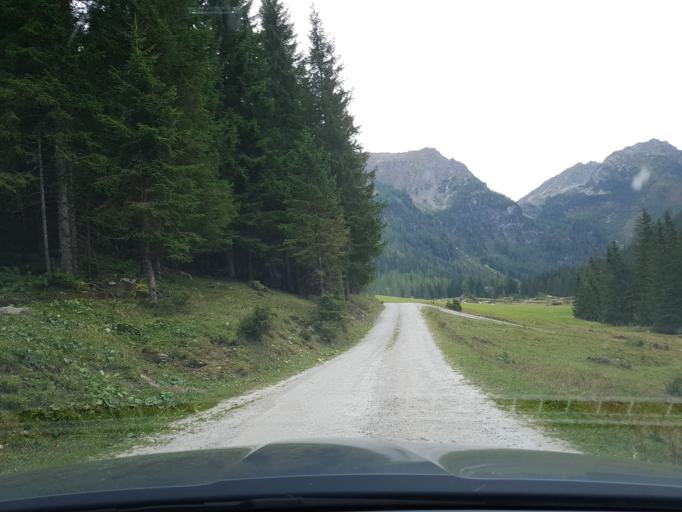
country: AT
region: Salzburg
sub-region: Politischer Bezirk Sankt Johann im Pongau
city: Untertauern
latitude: 47.2993
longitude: 13.5802
